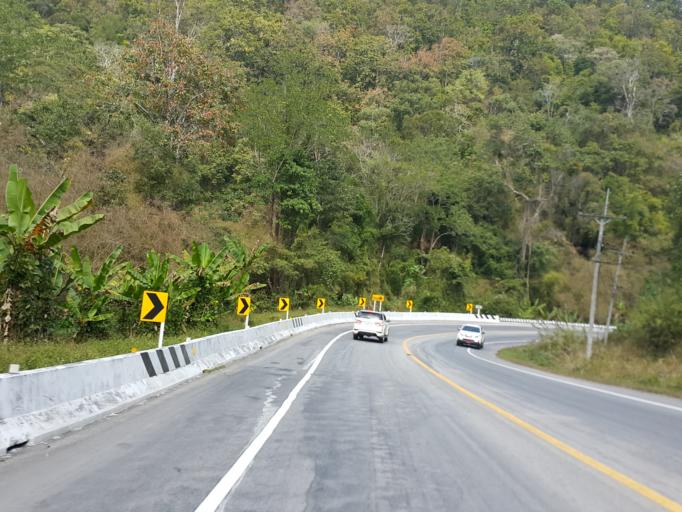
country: TH
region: Lampang
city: Wang Nuea
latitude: 19.0883
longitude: 99.4122
